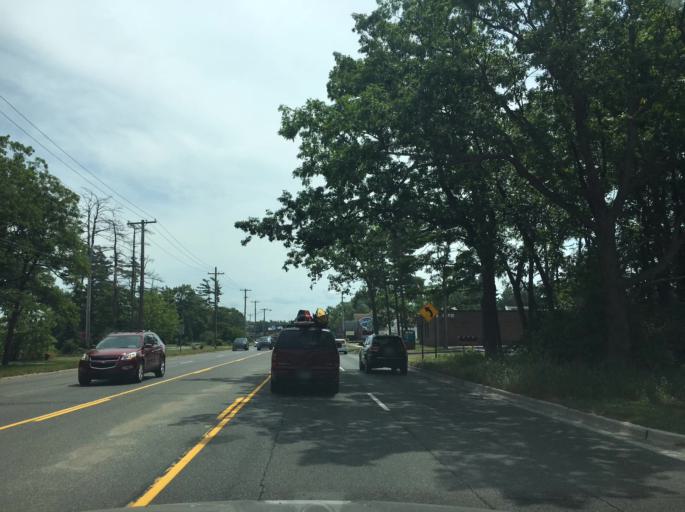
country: US
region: Michigan
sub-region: Grand Traverse County
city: Traverse City
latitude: 44.7505
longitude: -85.5627
